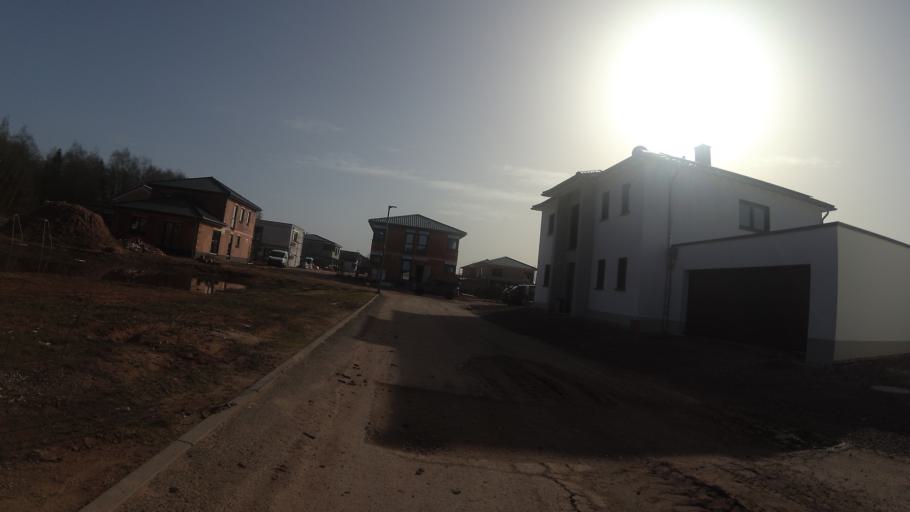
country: DE
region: Saarland
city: Uberherrn
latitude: 49.2759
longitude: 6.7135
